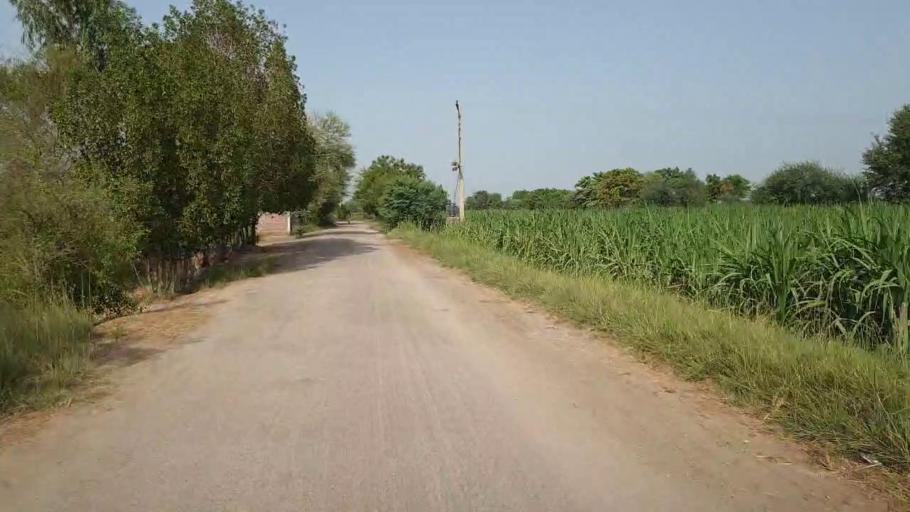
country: PK
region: Sindh
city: Daur
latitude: 26.3223
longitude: 68.1540
